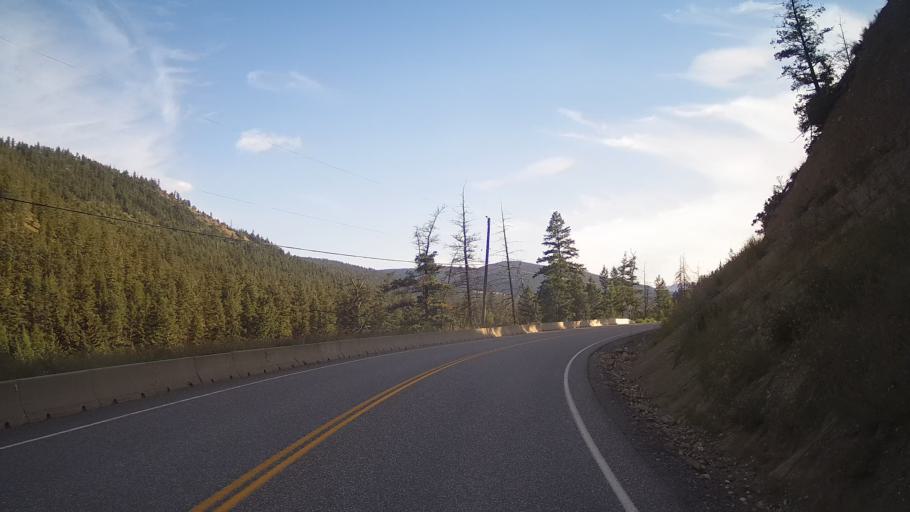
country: CA
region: British Columbia
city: Cache Creek
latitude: 50.8637
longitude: -121.5272
